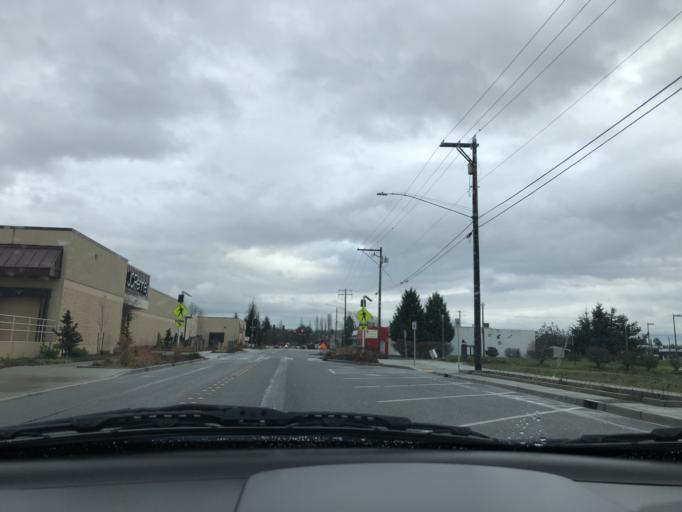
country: US
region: Washington
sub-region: Snohomish County
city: Marysville
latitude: 48.0491
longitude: -122.1795
